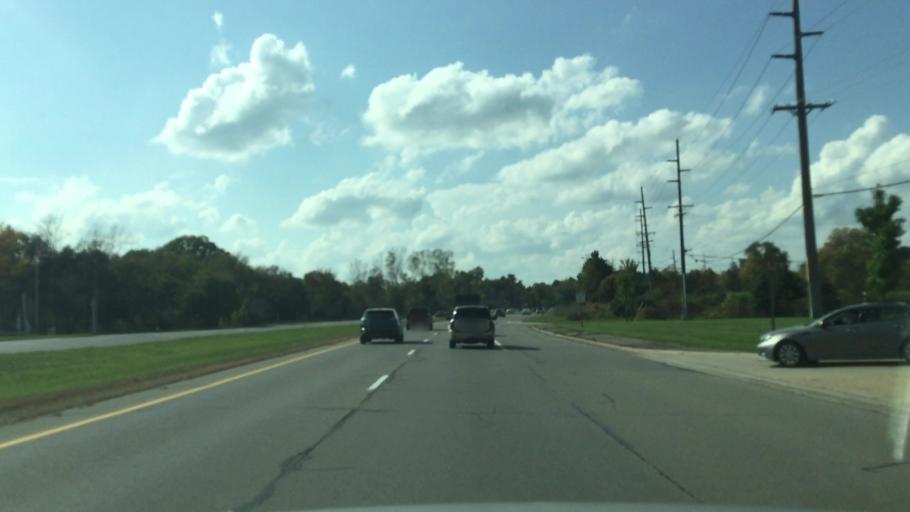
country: US
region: Michigan
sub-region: Oakland County
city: Milford
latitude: 42.6489
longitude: -83.5360
